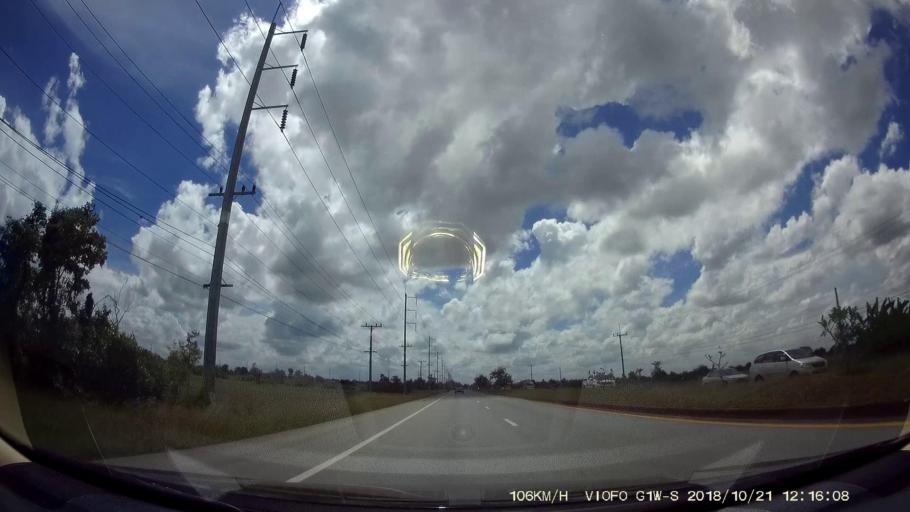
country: TH
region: Nakhon Ratchasima
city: Dan Khun Thot
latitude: 15.3518
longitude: 101.8270
